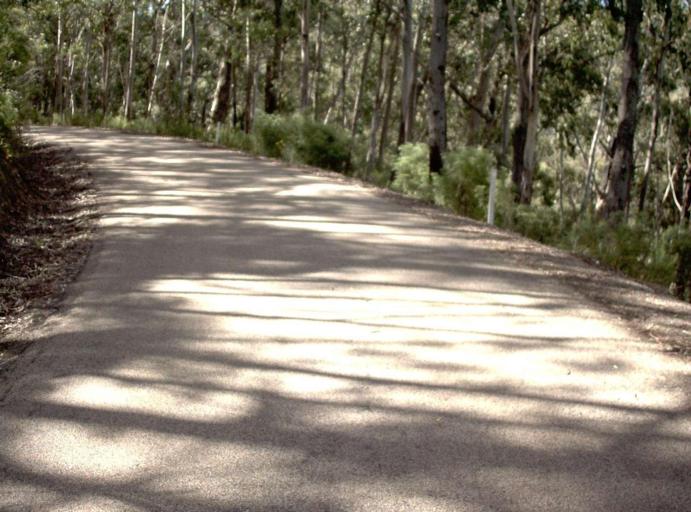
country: AU
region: Victoria
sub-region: East Gippsland
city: Lakes Entrance
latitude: -37.4008
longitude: 148.1249
